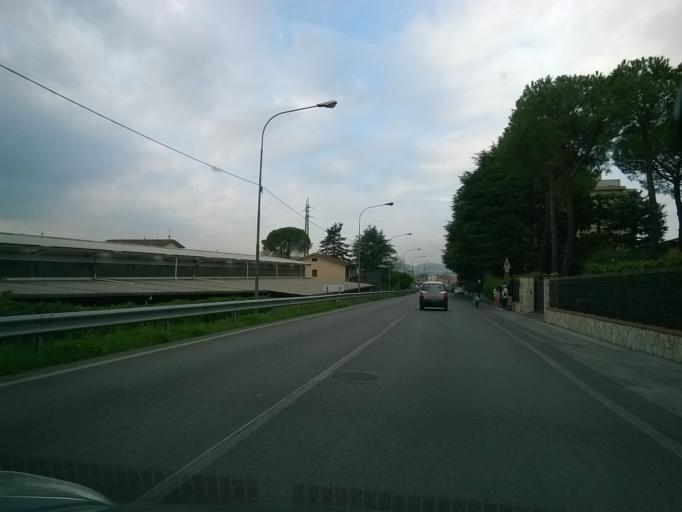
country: IT
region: Tuscany
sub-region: Provincia di Pistoia
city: Santa Lucia
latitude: 43.8803
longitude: 10.7085
